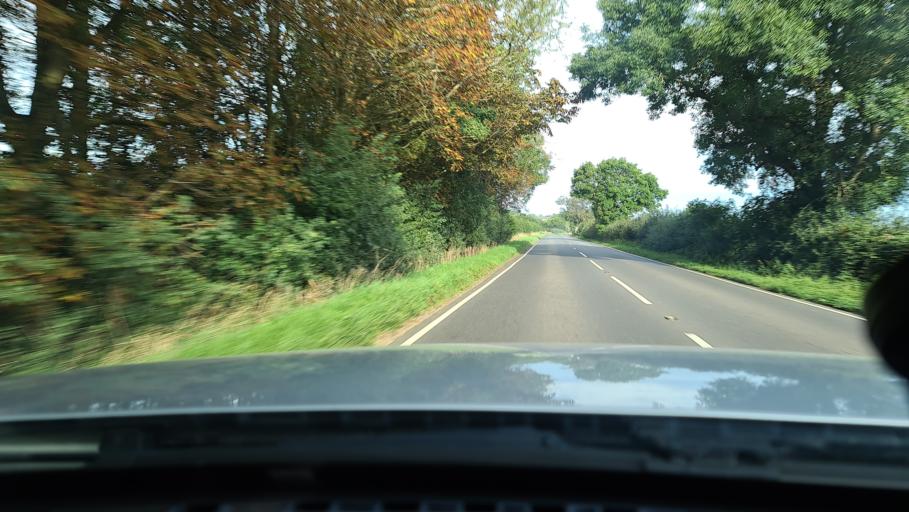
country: GB
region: England
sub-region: Warwickshire
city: Wellesbourne Mountford
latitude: 52.1153
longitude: -1.4891
